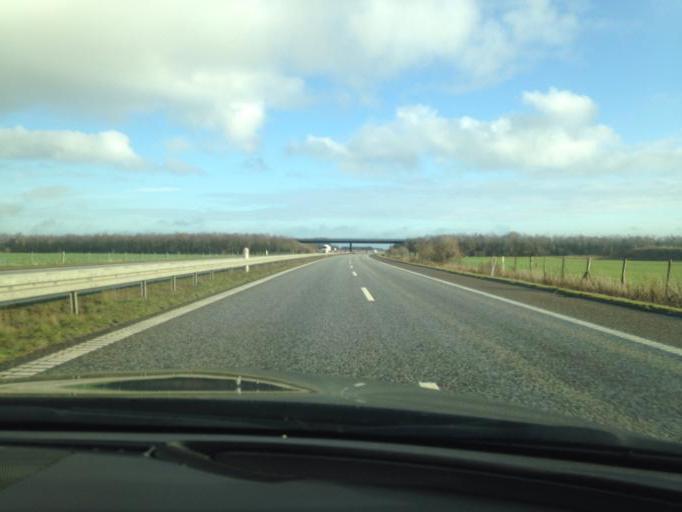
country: DK
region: South Denmark
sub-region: Vejen Kommune
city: Vejen
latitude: 55.4969
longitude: 9.2020
